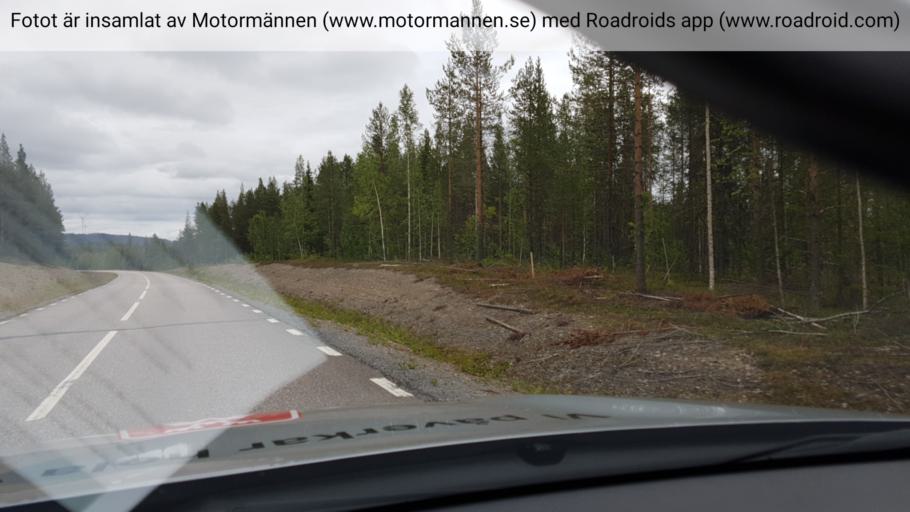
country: SE
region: Norrbotten
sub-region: Overkalix Kommun
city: OEverkalix
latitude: 67.0093
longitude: 21.8922
